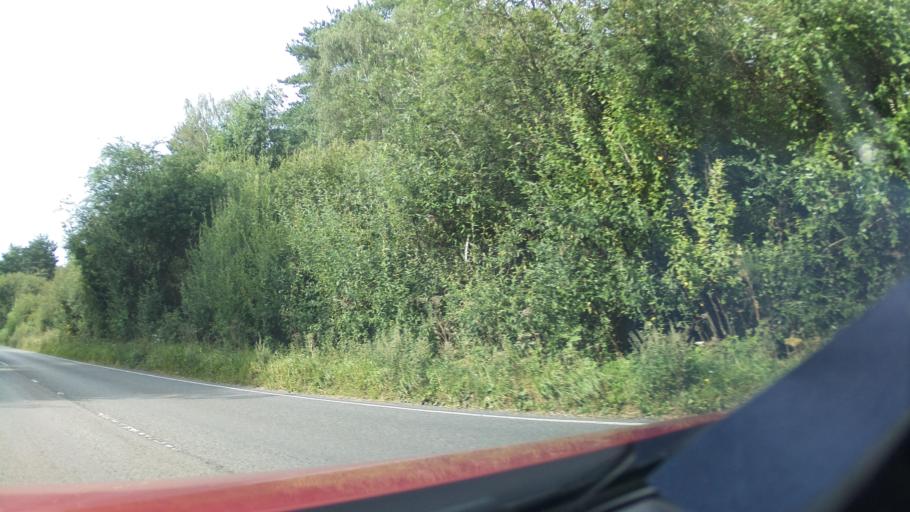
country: GB
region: England
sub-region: Hampshire
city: Hythe
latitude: 50.8580
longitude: -1.4282
